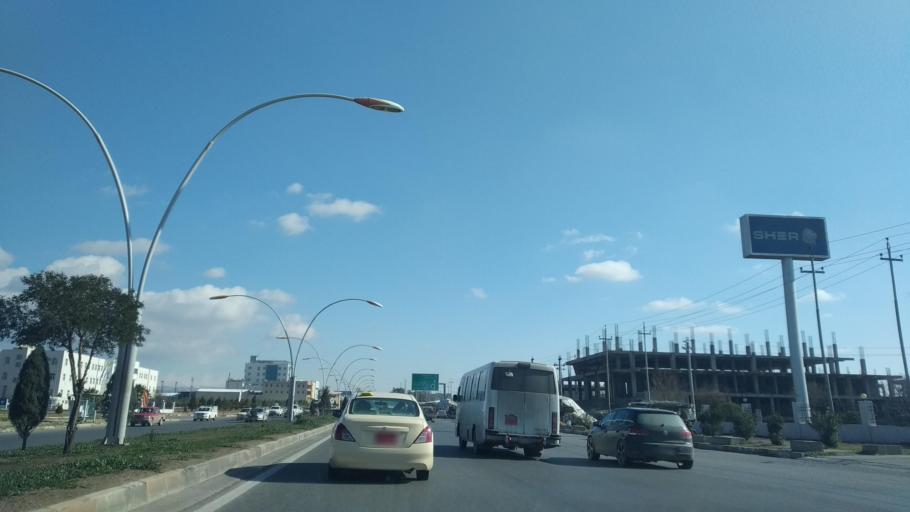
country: IQ
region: Arbil
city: Erbil
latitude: 36.1983
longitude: 44.0754
